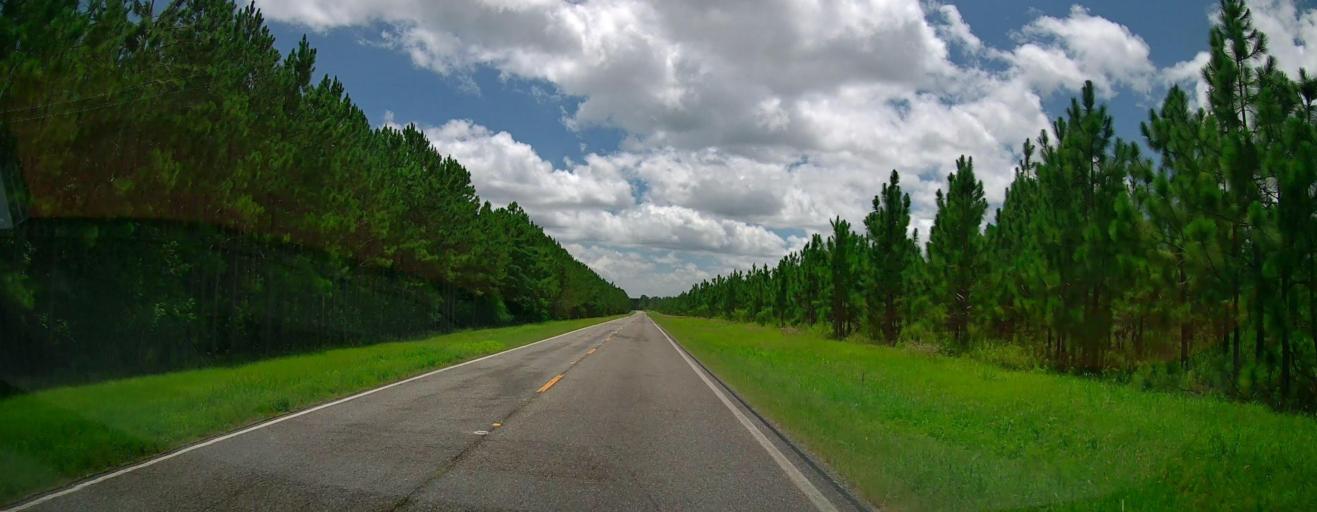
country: US
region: Georgia
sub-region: Wilcox County
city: Rochelle
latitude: 31.8687
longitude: -83.5584
